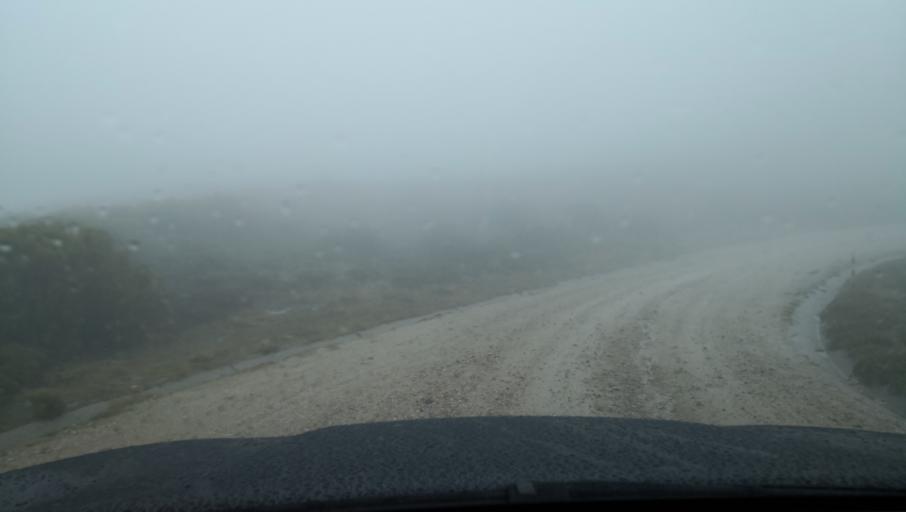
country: PT
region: Vila Real
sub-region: Vila Real
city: Vila Real
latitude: 41.3349
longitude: -7.8374
